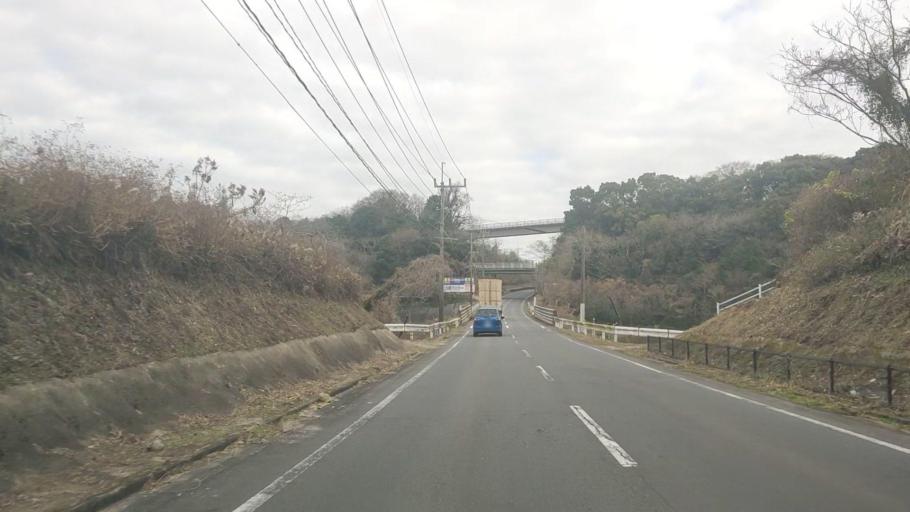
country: JP
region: Nagasaki
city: Shimabara
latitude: 32.8502
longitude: 130.2390
